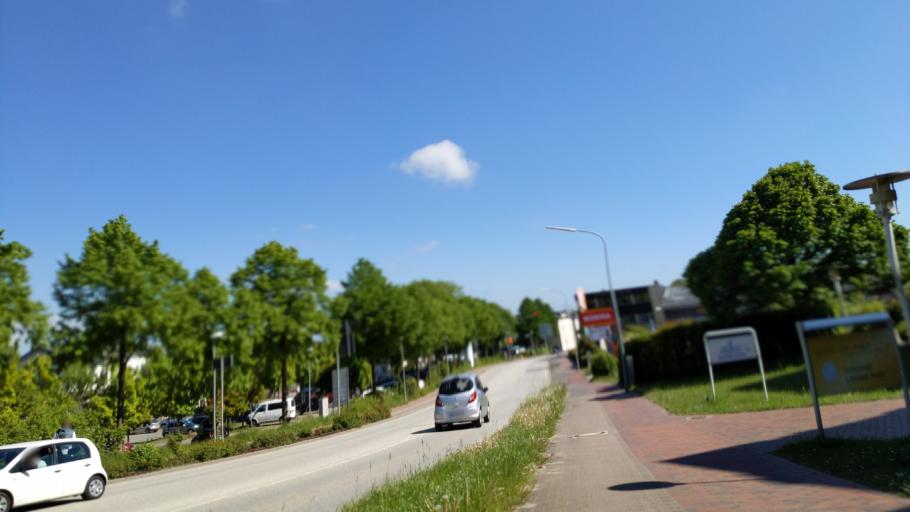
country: DE
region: Schleswig-Holstein
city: Eutin
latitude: 54.1361
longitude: 10.6079
